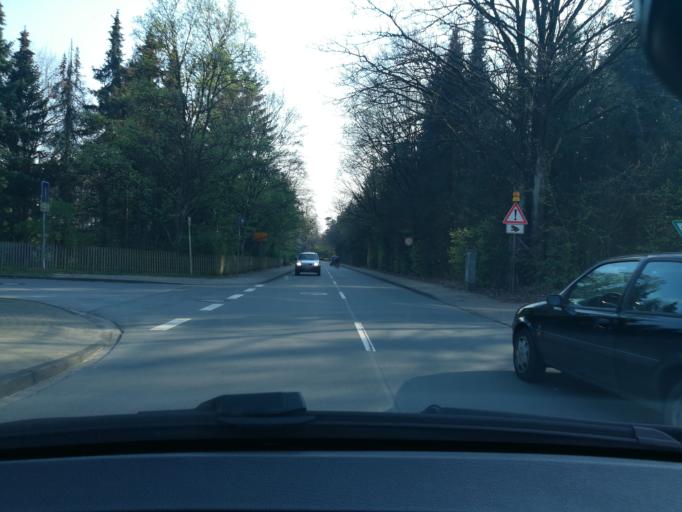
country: DE
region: North Rhine-Westphalia
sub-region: Regierungsbezirk Detmold
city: Bielefeld
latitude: 52.0043
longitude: 8.4758
